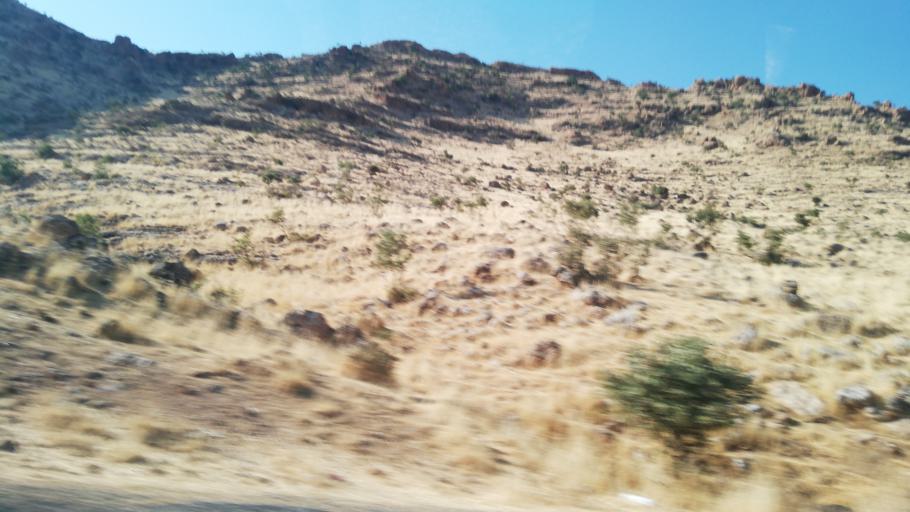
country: TR
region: Mardin
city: Sivrice
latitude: 37.2488
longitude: 41.3505
